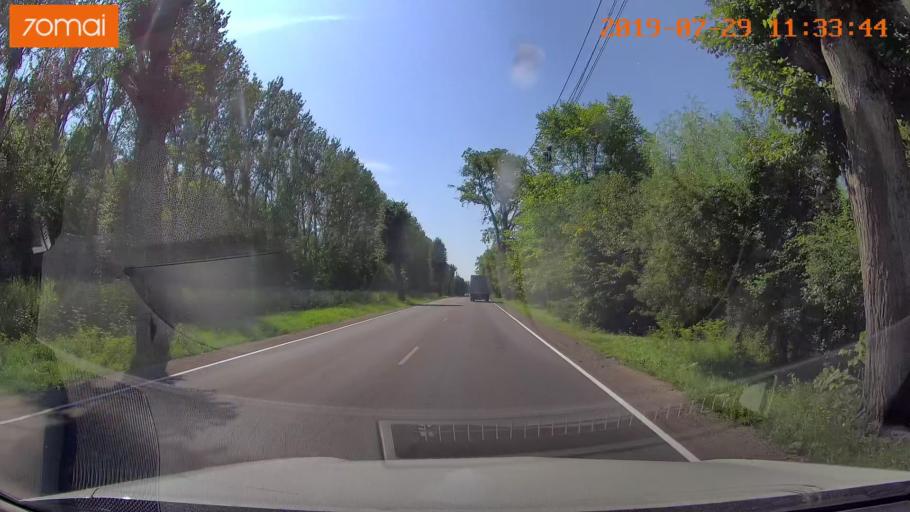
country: RU
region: Kaliningrad
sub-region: Gorod Kaliningrad
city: Kaliningrad
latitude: 54.6621
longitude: 20.5407
